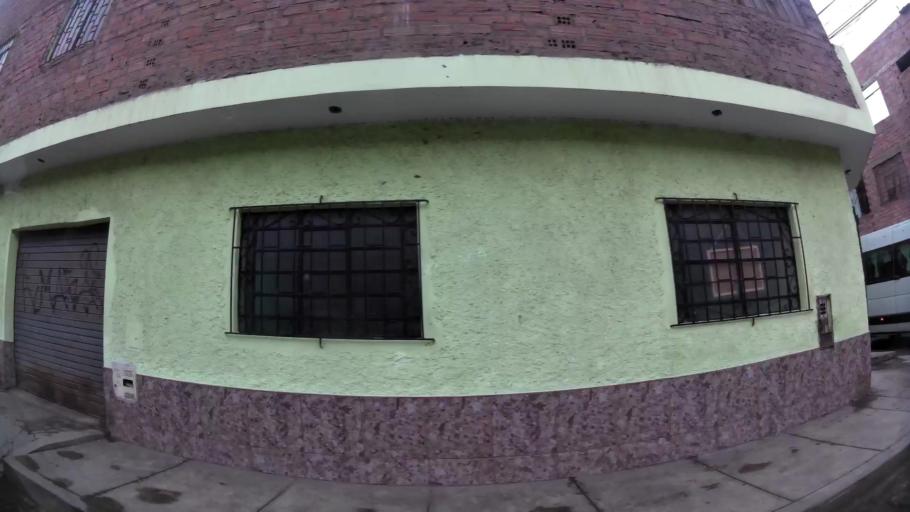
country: PE
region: Lima
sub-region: Lima
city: San Luis
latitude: -12.0527
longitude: -77.0018
